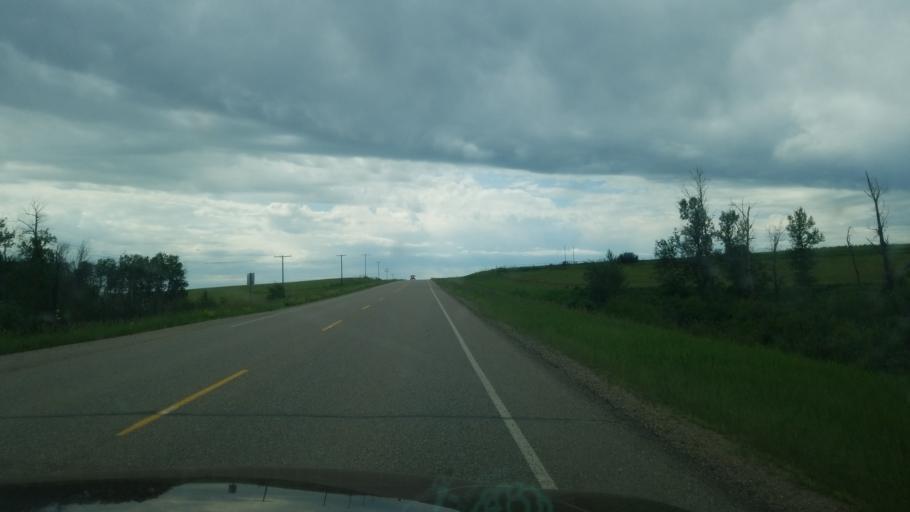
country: CA
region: Saskatchewan
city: Unity
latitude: 52.9734
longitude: -109.3426
